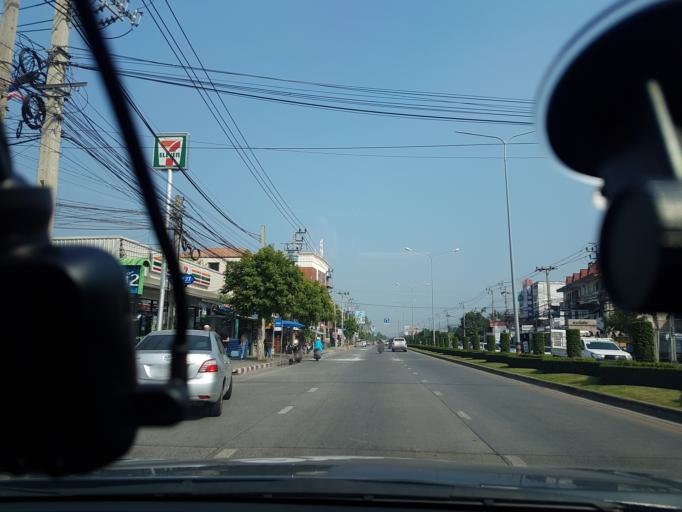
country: TH
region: Bangkok
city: Khlong Sam Wa
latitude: 13.8615
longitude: 100.7169
